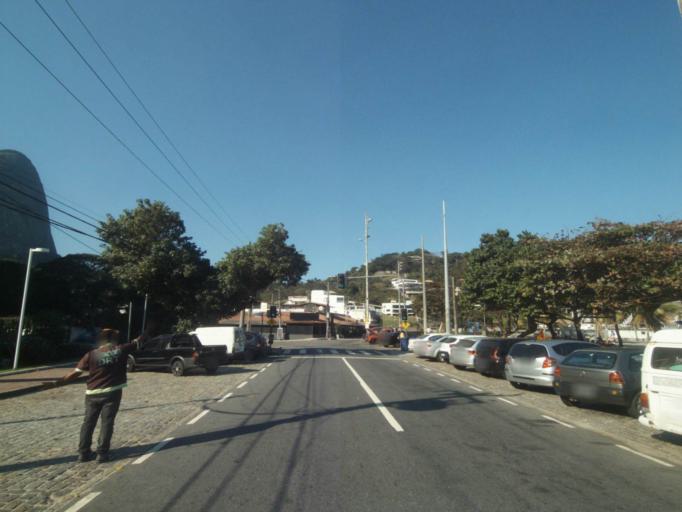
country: BR
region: Rio de Janeiro
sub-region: Rio De Janeiro
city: Rio de Janeiro
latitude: -23.0143
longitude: -43.2983
